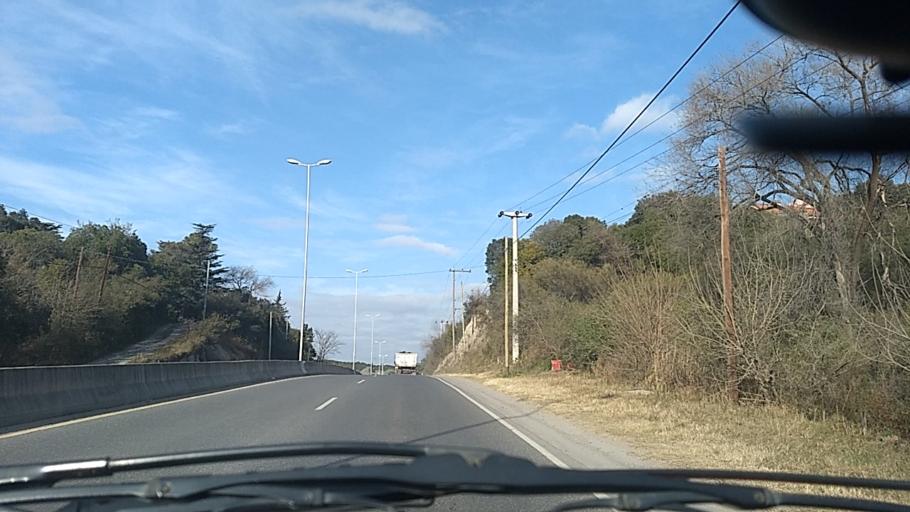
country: AR
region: Cordoba
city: Salsipuedes
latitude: -31.1498
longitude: -64.2986
